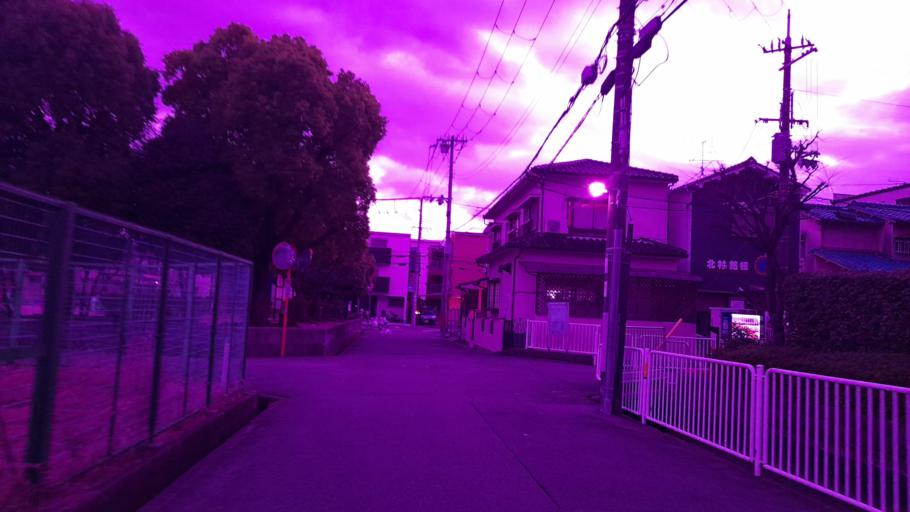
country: JP
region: Hyogo
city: Amagasaki
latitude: 34.7459
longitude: 135.4351
